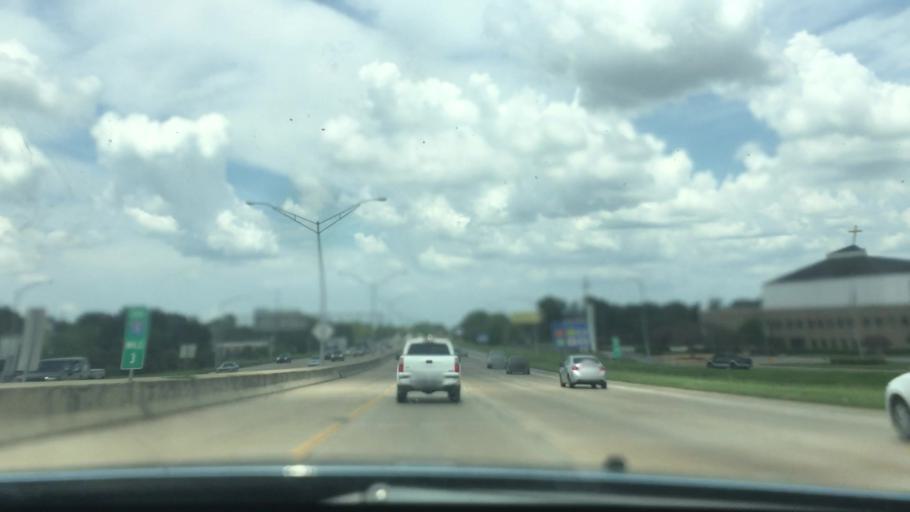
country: US
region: Louisiana
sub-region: East Baton Rouge Parish
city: Westminster
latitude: 30.4246
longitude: -91.0731
